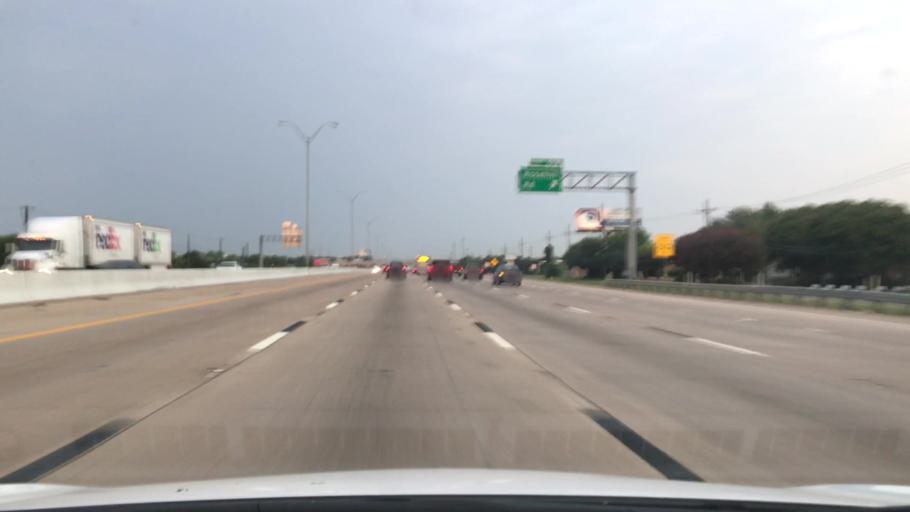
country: US
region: Texas
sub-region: Dallas County
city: Sunnyvale
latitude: 32.8482
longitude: -96.5756
